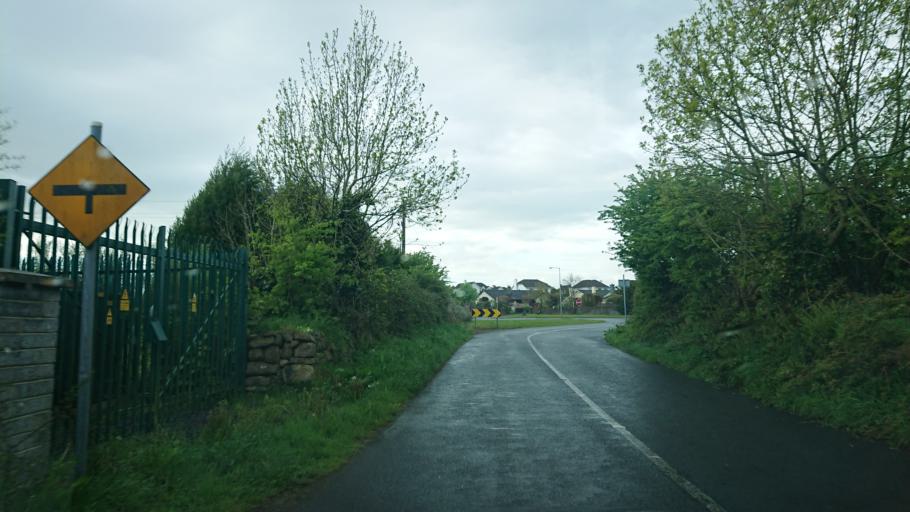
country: IE
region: Munster
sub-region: Waterford
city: Waterford
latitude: 52.2352
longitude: -7.0792
